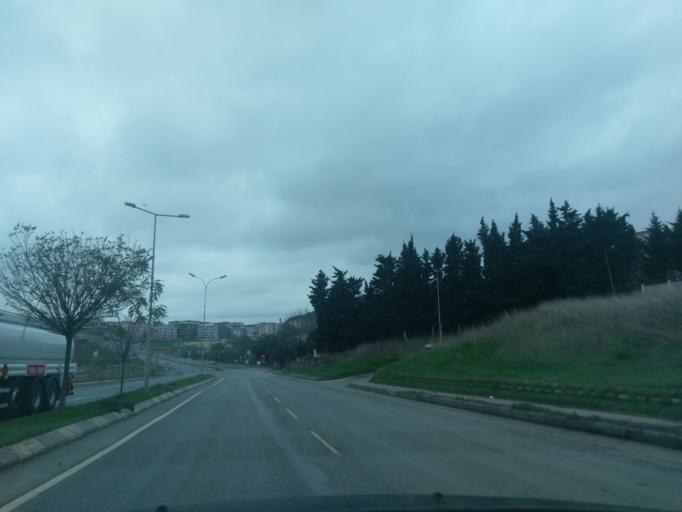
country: TR
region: Istanbul
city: Catalca
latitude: 41.1529
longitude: 28.4569
